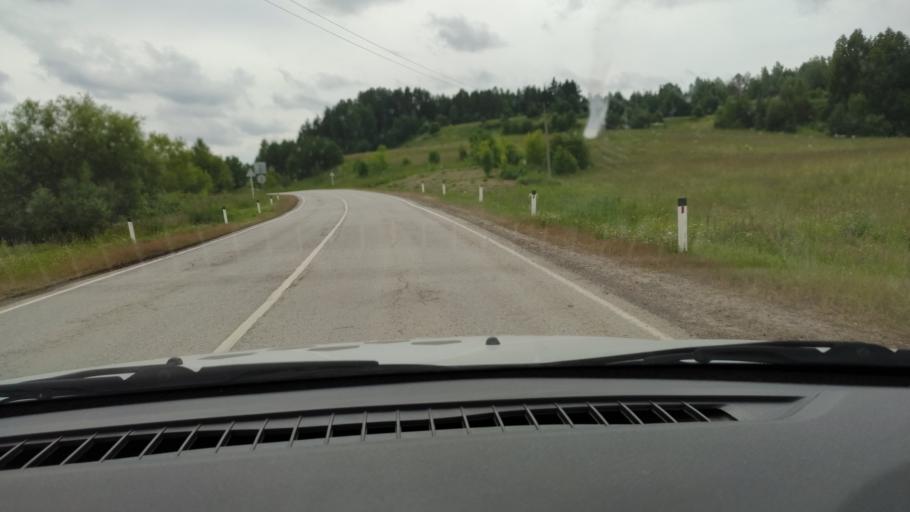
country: RU
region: Perm
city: Kukushtan
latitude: 57.4972
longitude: 56.6441
